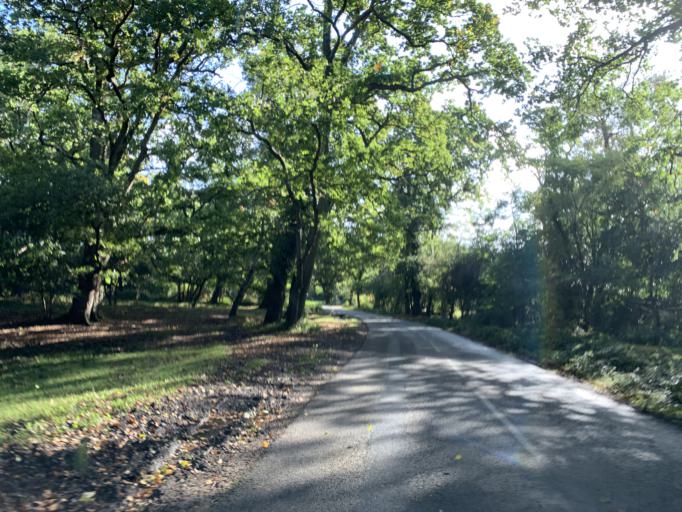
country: GB
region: England
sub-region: Hampshire
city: Brockenhurst
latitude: 50.8231
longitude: -1.5906
